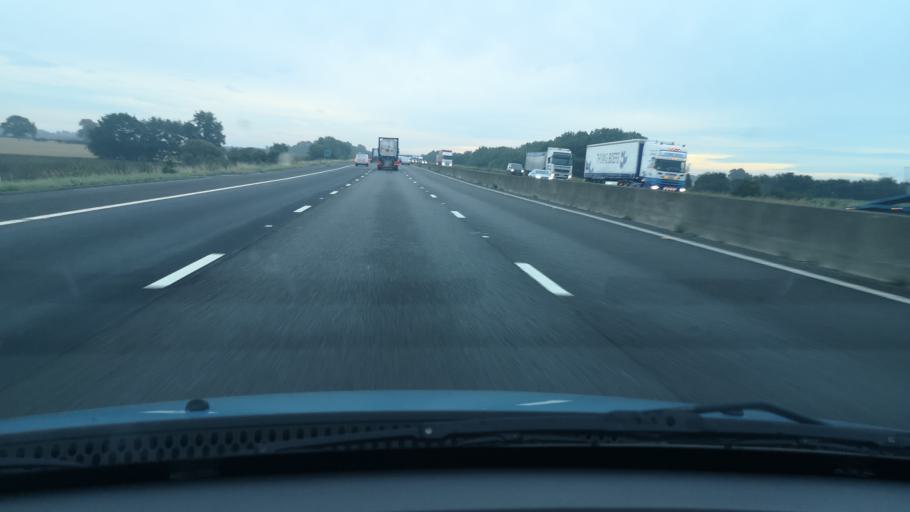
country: GB
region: England
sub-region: East Riding of Yorkshire
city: Rawcliffe
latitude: 53.6579
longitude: -0.9647
